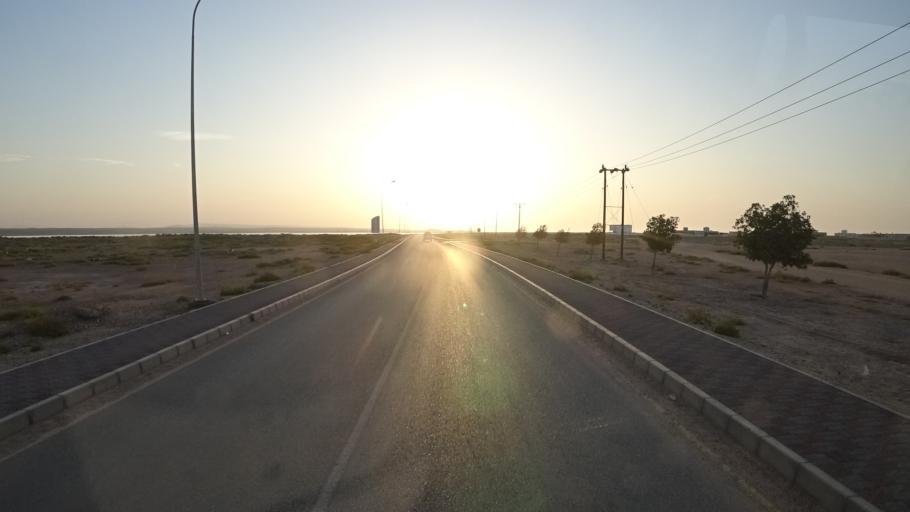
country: OM
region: Ash Sharqiyah
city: Sur
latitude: 22.5268
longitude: 59.7875
